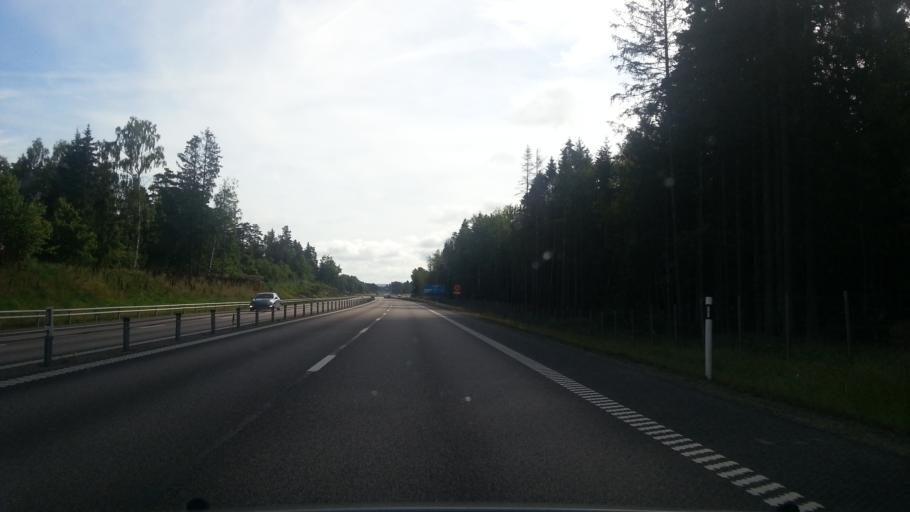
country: SE
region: Vaestra Goetaland
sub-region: Trollhattan
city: Sjuntorp
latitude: 58.2423
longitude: 12.2509
